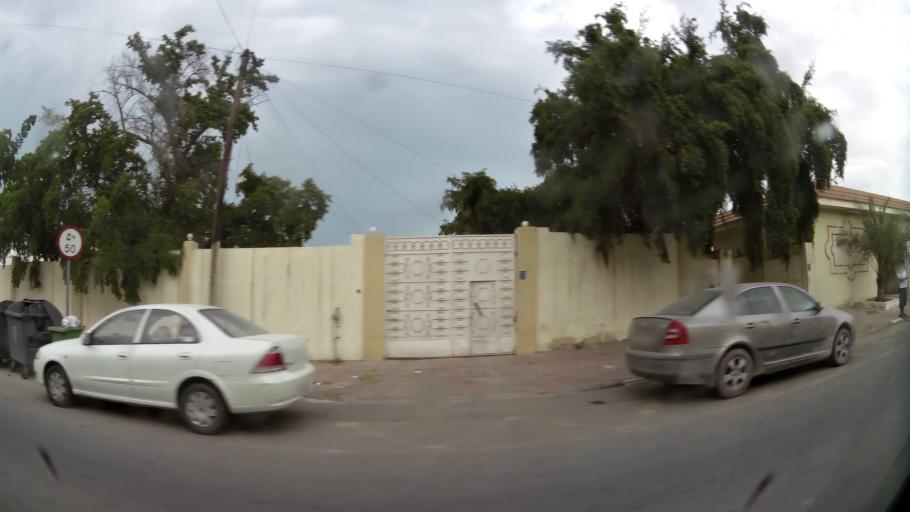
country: QA
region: Baladiyat ad Dawhah
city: Doha
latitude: 25.2687
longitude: 51.5007
